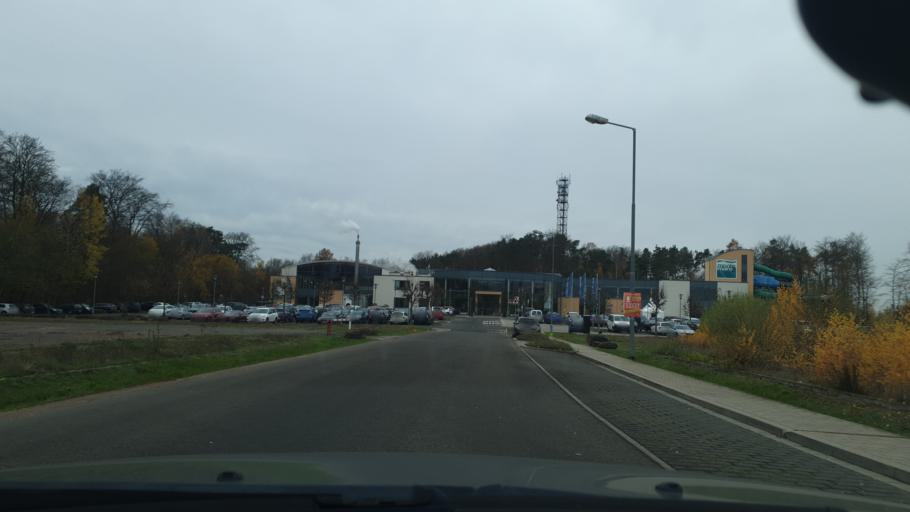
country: DE
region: Rheinland-Pfalz
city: Kaiserslautern
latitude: 49.4541
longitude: 7.8128
